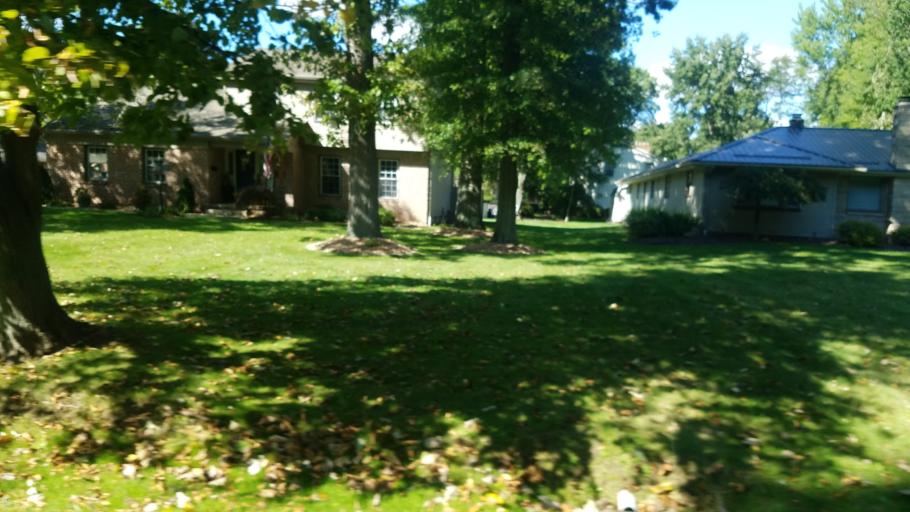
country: US
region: Ohio
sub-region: Mahoning County
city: Boardman
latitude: 41.0467
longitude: -80.6916
